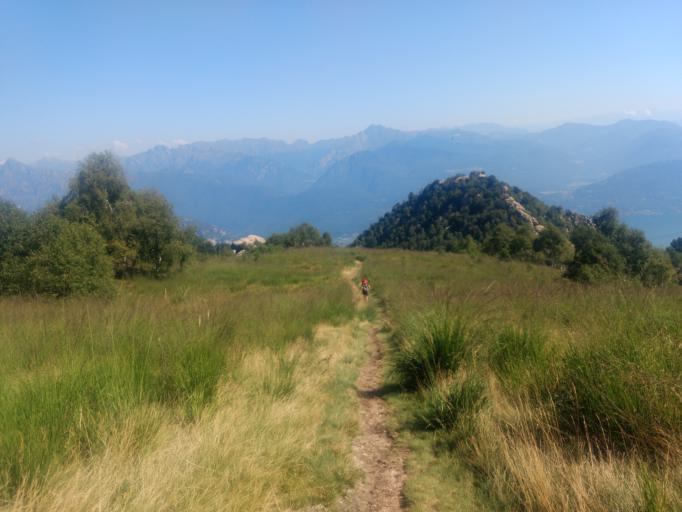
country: IT
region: Piedmont
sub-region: Provincia Verbano-Cusio-Ossola
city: Gabbio-Cereda-Ramate
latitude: 45.8909
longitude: 8.4560
